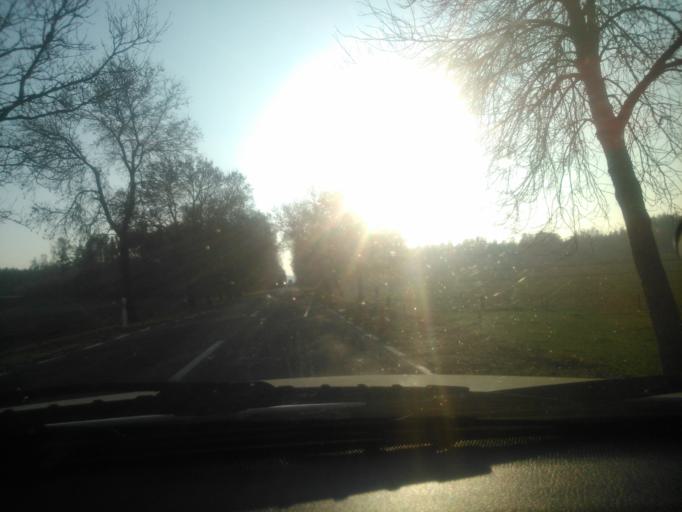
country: PL
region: Masovian Voivodeship
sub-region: Powiat przasnyski
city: Krzynowloga Mala
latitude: 53.1816
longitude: 20.8258
